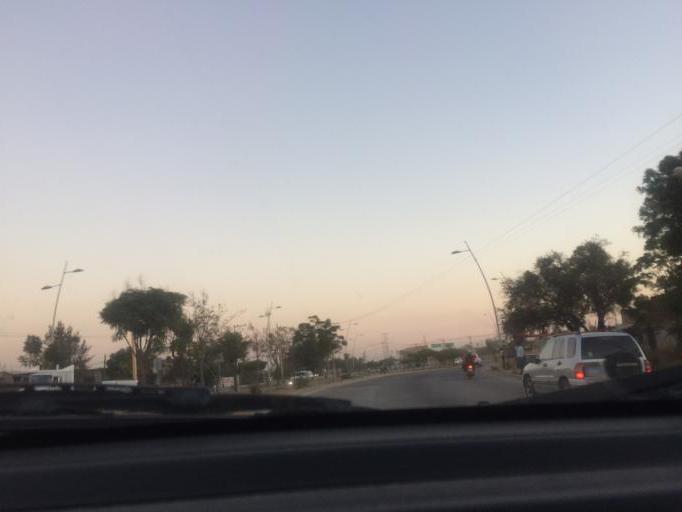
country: MX
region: Guanajuato
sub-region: Leon
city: Fraccionamiento Paraiso Real
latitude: 21.1284
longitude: -101.6001
